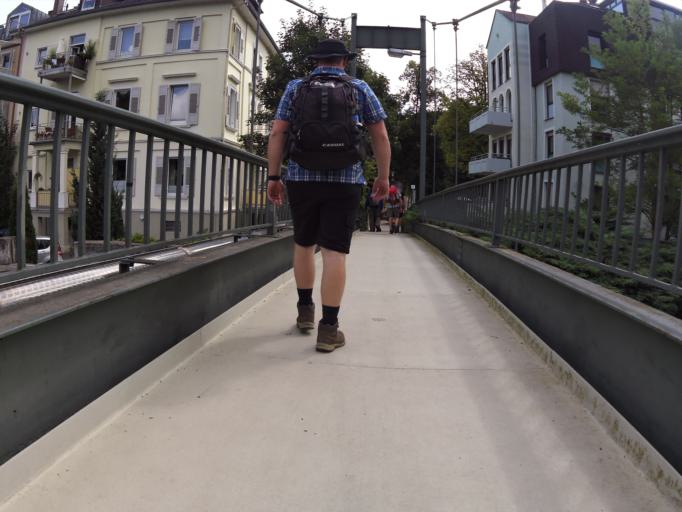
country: DE
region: Rheinland-Pfalz
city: Bad Kreuznach
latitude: 49.8380
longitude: 7.8516
